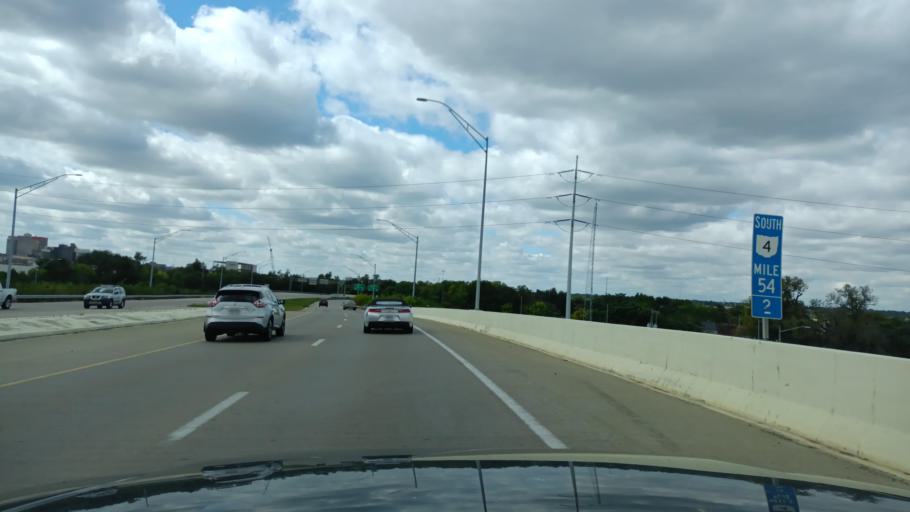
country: US
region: Ohio
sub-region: Montgomery County
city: Dayton
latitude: 39.7718
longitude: -84.1787
